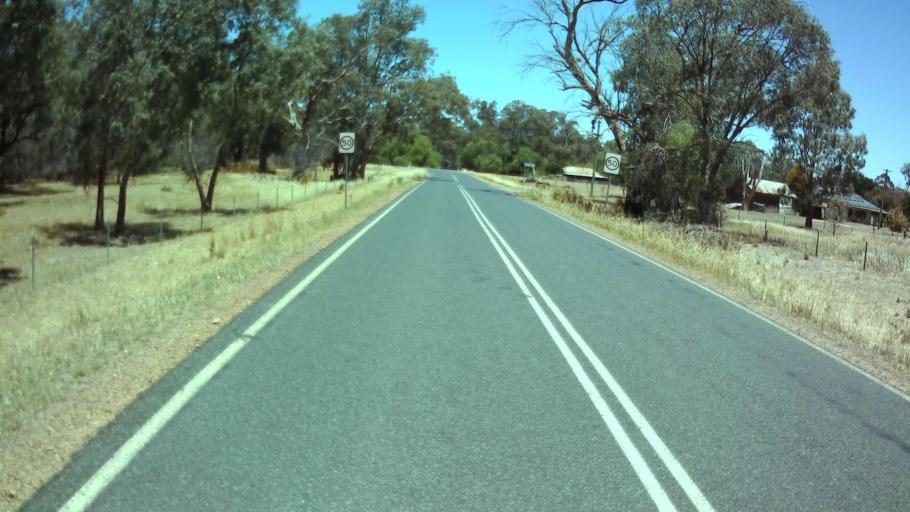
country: AU
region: New South Wales
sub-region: Weddin
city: Grenfell
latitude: -34.0382
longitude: 147.9311
